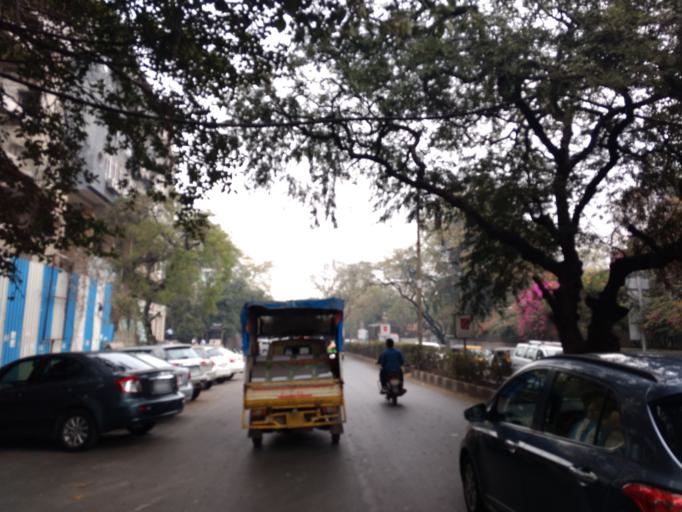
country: IN
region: Maharashtra
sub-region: Pune Division
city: Pune
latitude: 18.5220
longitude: 73.8778
